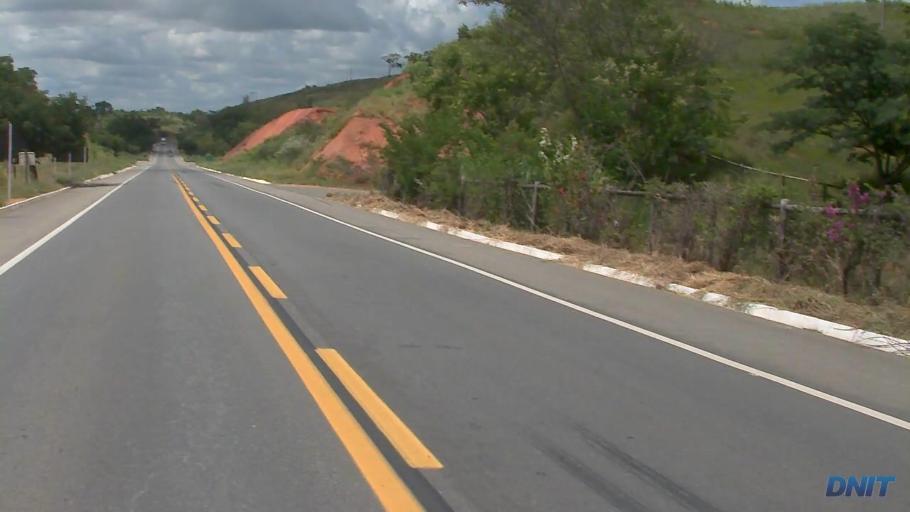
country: BR
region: Minas Gerais
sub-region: Governador Valadares
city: Governador Valadares
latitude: -18.9197
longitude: -42.0148
